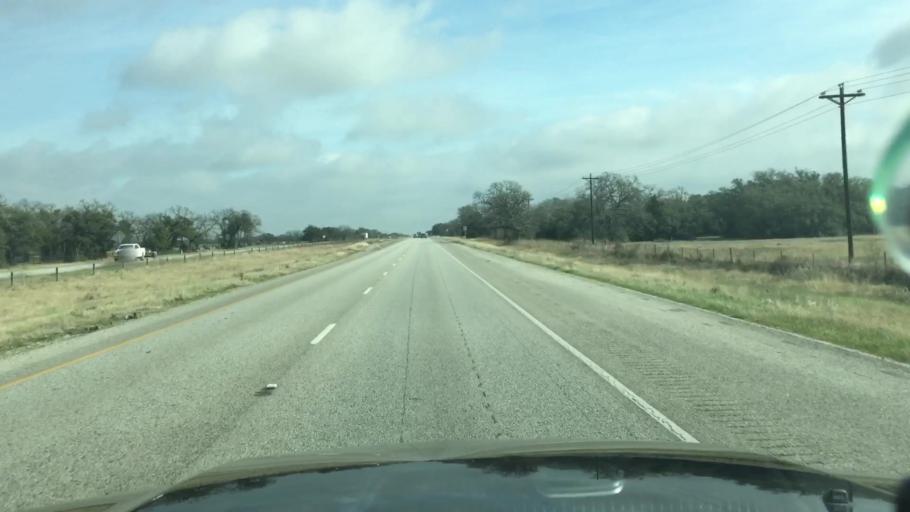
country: US
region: Texas
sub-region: Lee County
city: Giddings
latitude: 30.1744
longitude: -96.8864
